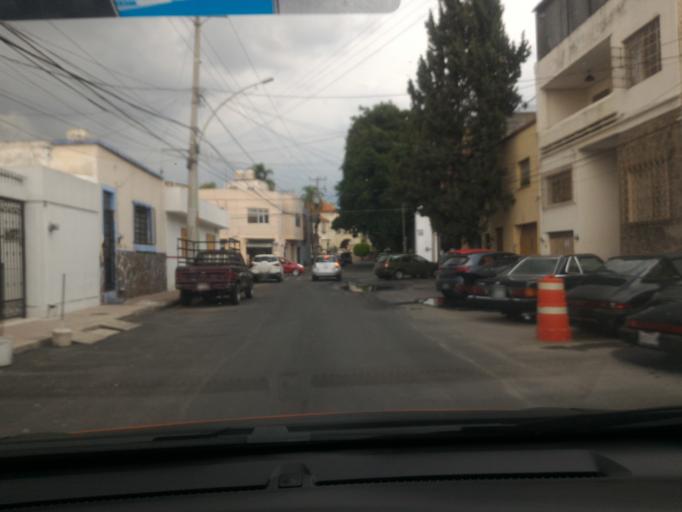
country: MX
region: Jalisco
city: Guadalajara
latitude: 20.6689
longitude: -103.3633
